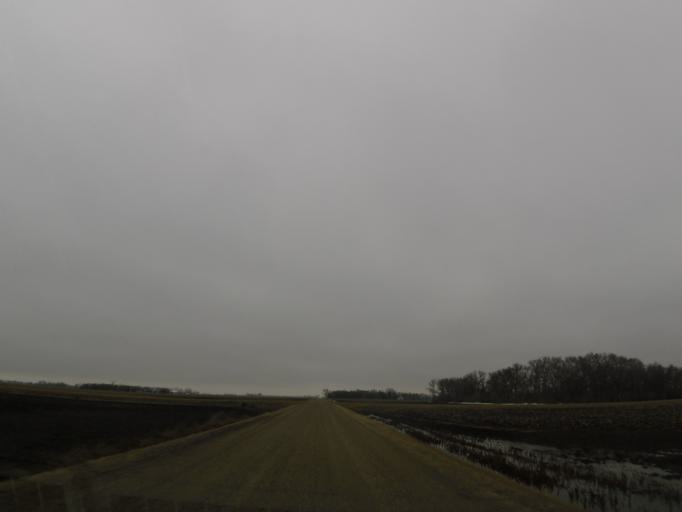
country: US
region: North Dakota
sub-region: Walsh County
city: Grafton
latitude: 48.3965
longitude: -97.2119
